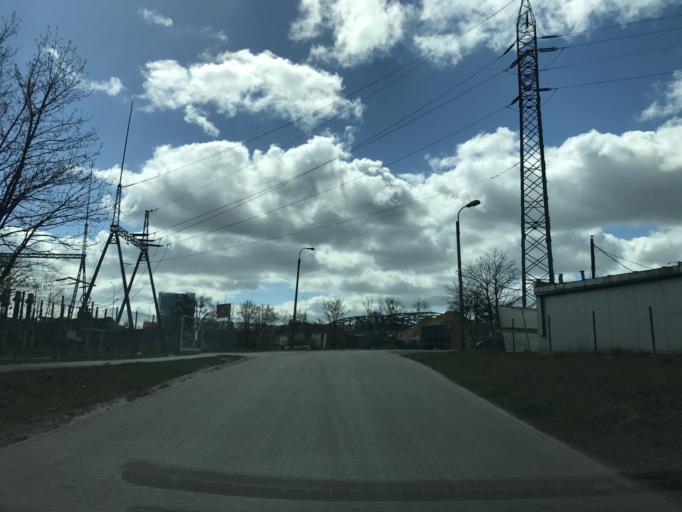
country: PL
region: Pomeranian Voivodeship
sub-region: Gdansk
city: Gdansk
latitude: 54.3867
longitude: 18.6005
